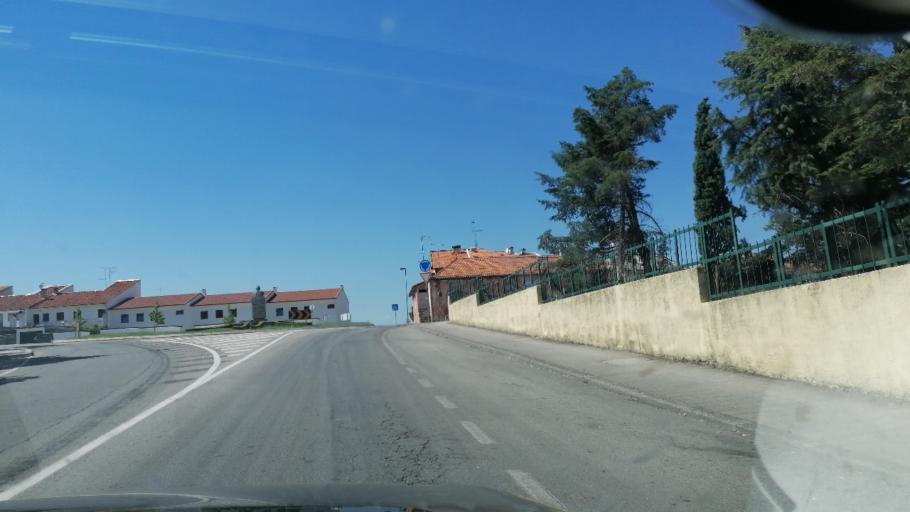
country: PT
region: Braganca
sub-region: Braganca Municipality
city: Braganca
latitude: 41.8095
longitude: -6.7552
